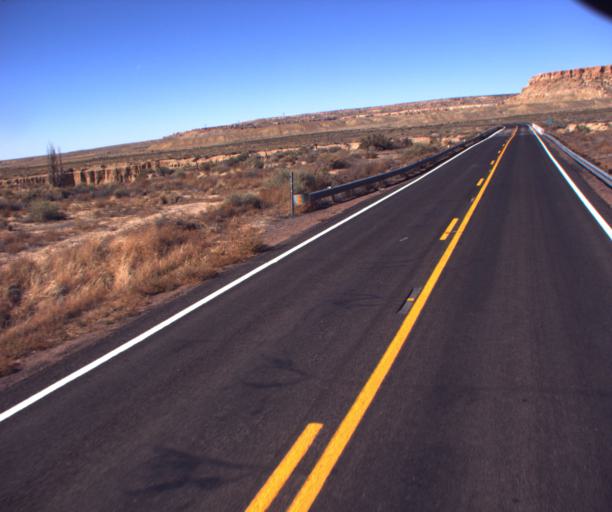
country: US
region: Arizona
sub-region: Navajo County
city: First Mesa
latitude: 35.9822
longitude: -110.7063
